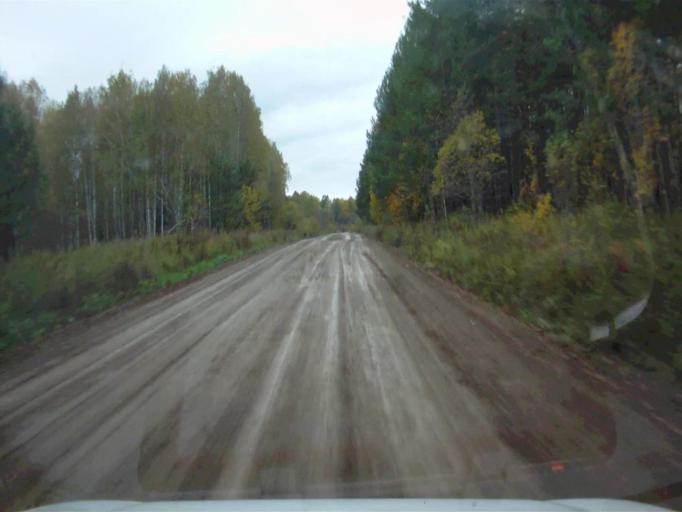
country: RU
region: Chelyabinsk
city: Nyazepetrovsk
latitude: 56.0983
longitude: 59.3942
